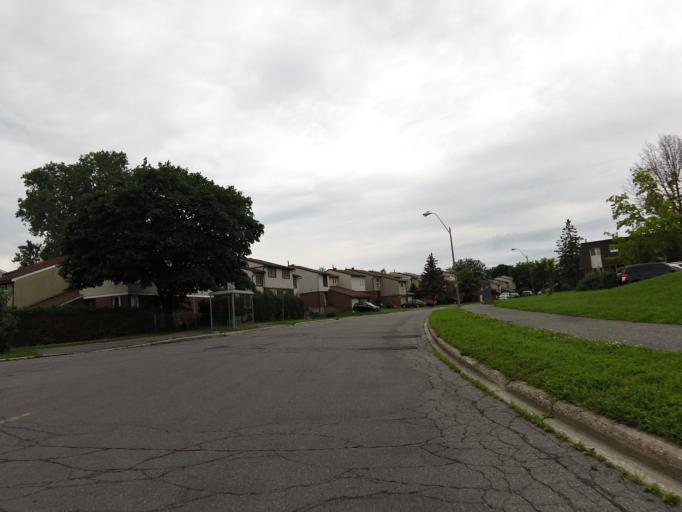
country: CA
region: Ontario
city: Bells Corners
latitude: 45.3473
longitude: -75.7966
